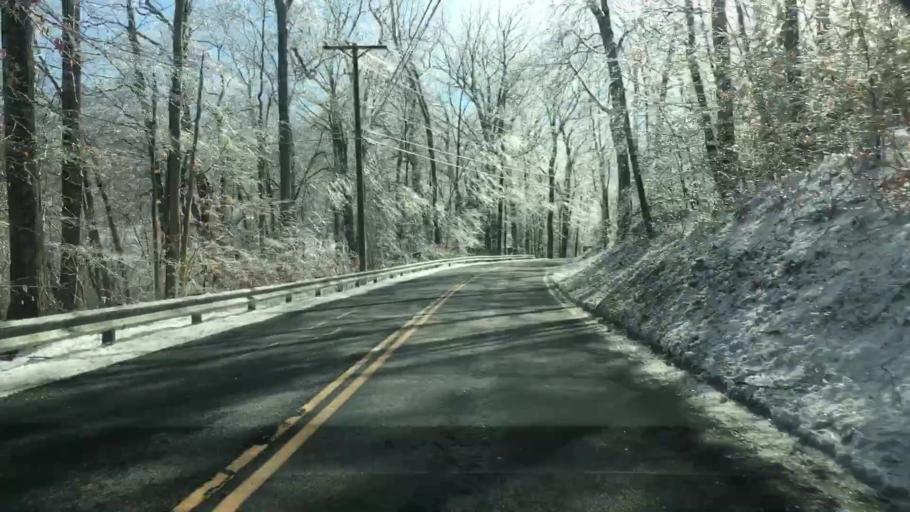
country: US
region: Connecticut
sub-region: Fairfield County
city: Newtown
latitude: 41.3502
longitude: -73.2327
